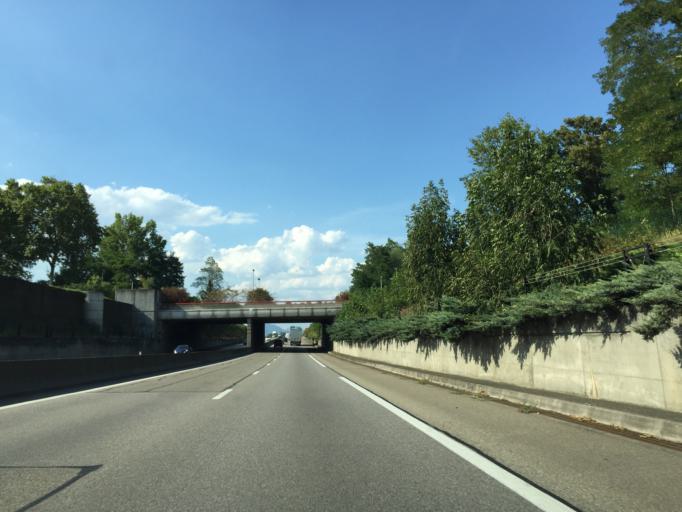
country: FR
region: Alsace
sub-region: Departement du Haut-Rhin
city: Horbourg-Wihr
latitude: 48.0800
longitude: 7.3848
